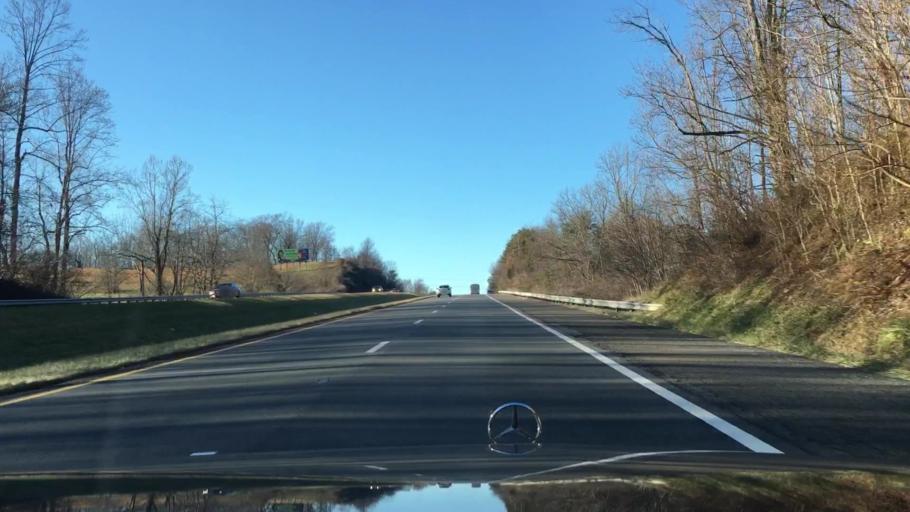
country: US
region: Virginia
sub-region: Montgomery County
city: Christiansburg
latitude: 37.1464
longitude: -80.3931
